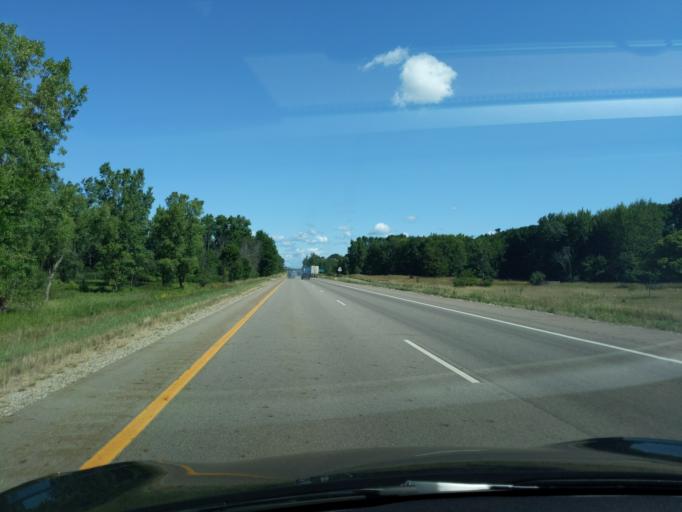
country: US
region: Michigan
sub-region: Gratiot County
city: Ithaca
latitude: 43.3263
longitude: -84.6010
